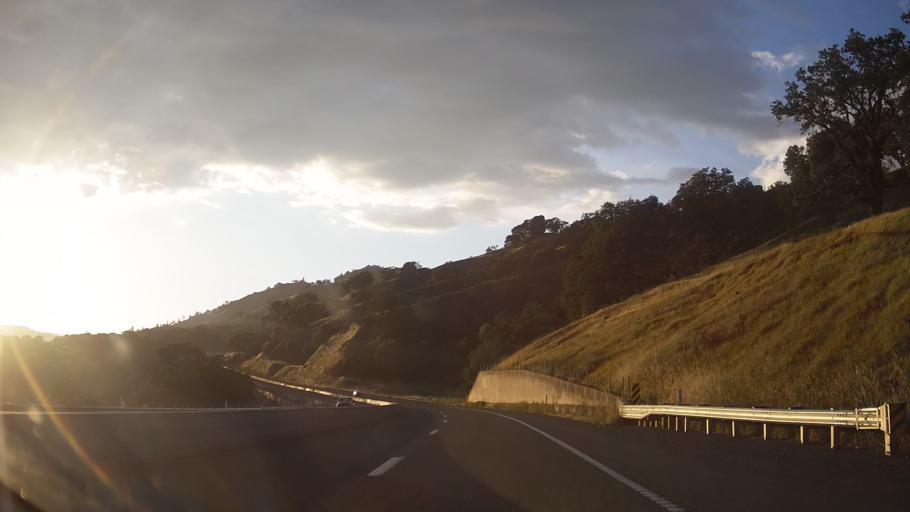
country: US
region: California
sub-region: Mendocino County
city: Redwood Valley
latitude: 39.2875
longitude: -123.2639
